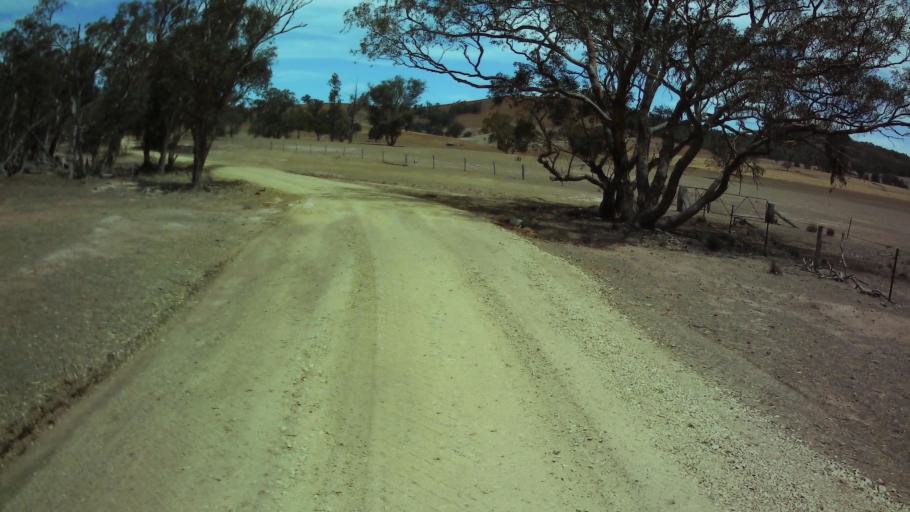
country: AU
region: New South Wales
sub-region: Weddin
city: Grenfell
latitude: -33.7836
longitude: 148.1517
